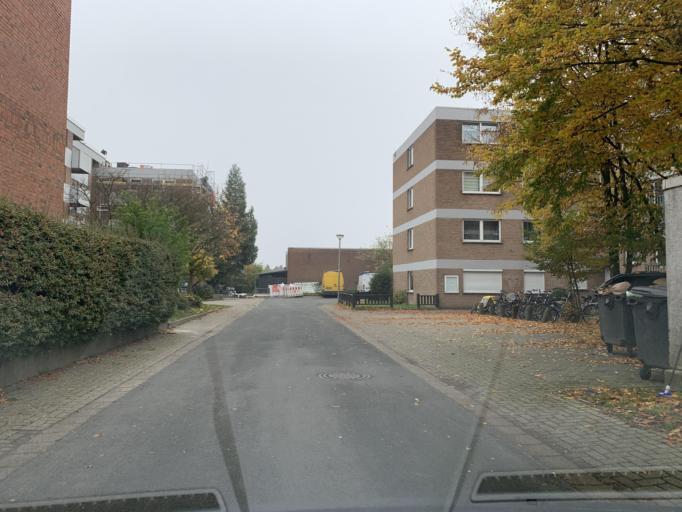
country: DE
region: North Rhine-Westphalia
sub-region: Regierungsbezirk Munster
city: Steinfurt
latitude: 52.1568
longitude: 7.3257
